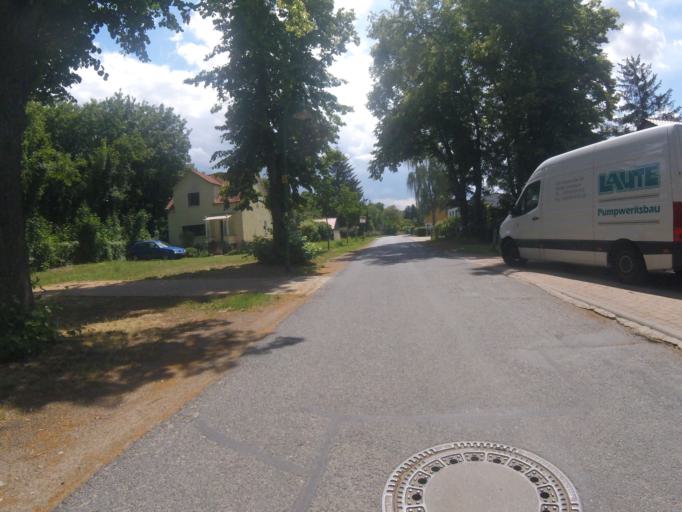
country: DE
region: Brandenburg
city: Bestensee
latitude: 52.2730
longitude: 13.6414
